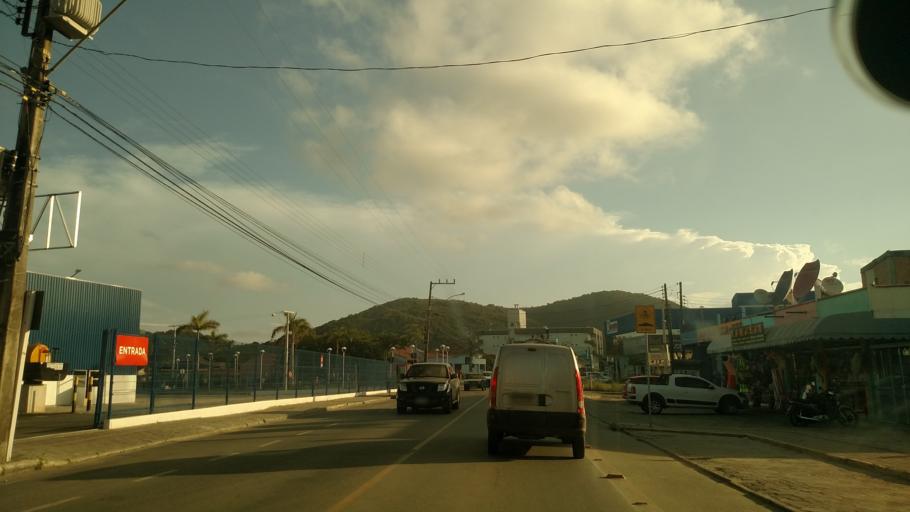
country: BR
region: Santa Catarina
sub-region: Porto Belo
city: Porto Belo
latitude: -27.1496
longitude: -48.5065
